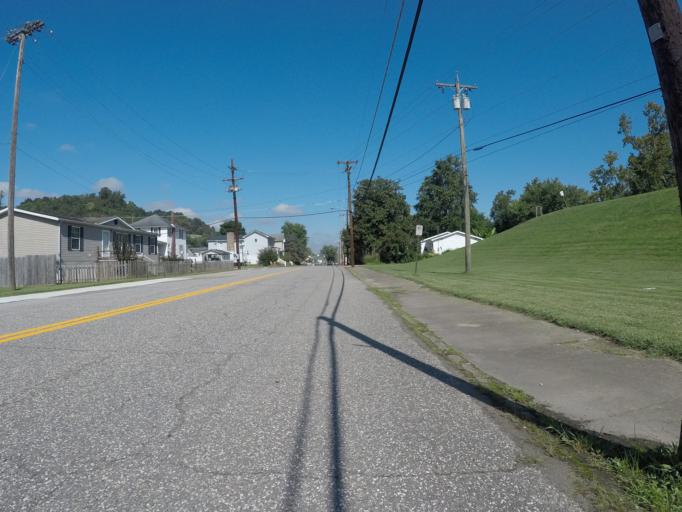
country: US
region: Ohio
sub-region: Lawrence County
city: South Point
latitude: 38.4200
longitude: -82.5985
